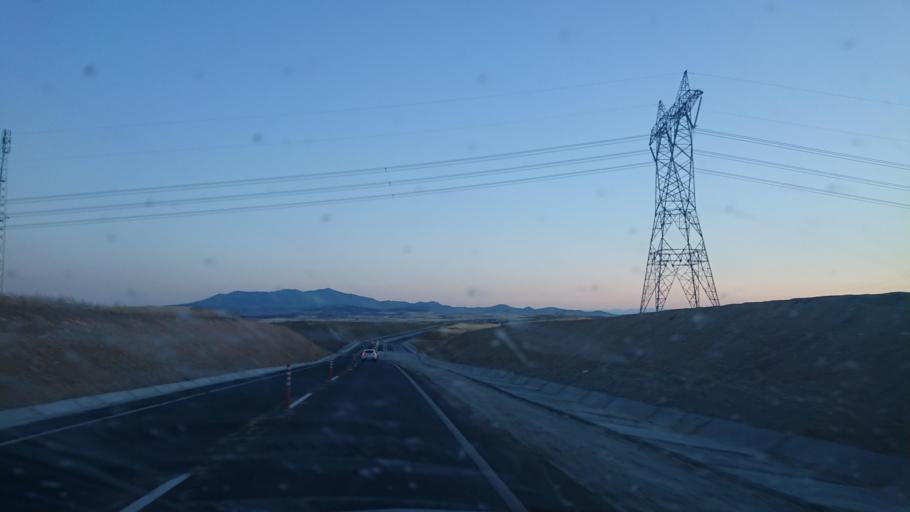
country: TR
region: Aksaray
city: Balci
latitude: 38.7849
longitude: 34.1190
